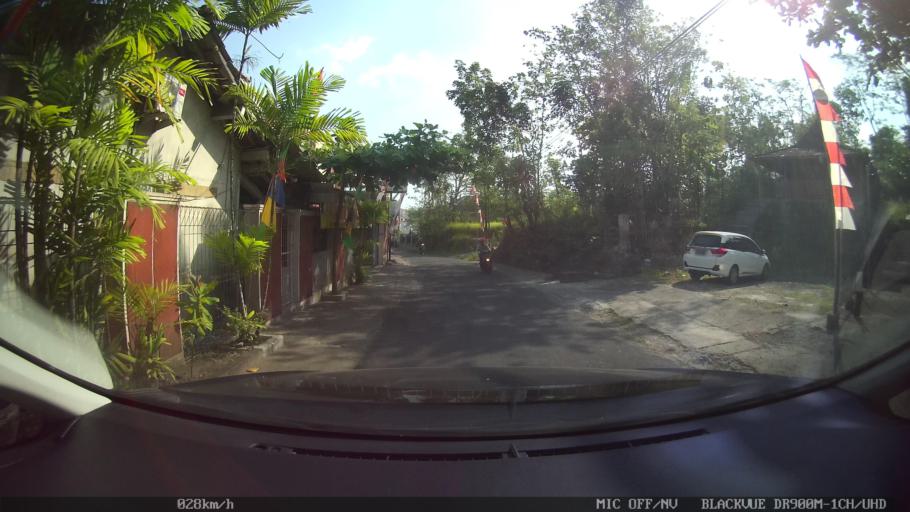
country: ID
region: Daerah Istimewa Yogyakarta
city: Kasihan
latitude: -7.8386
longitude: 110.3353
